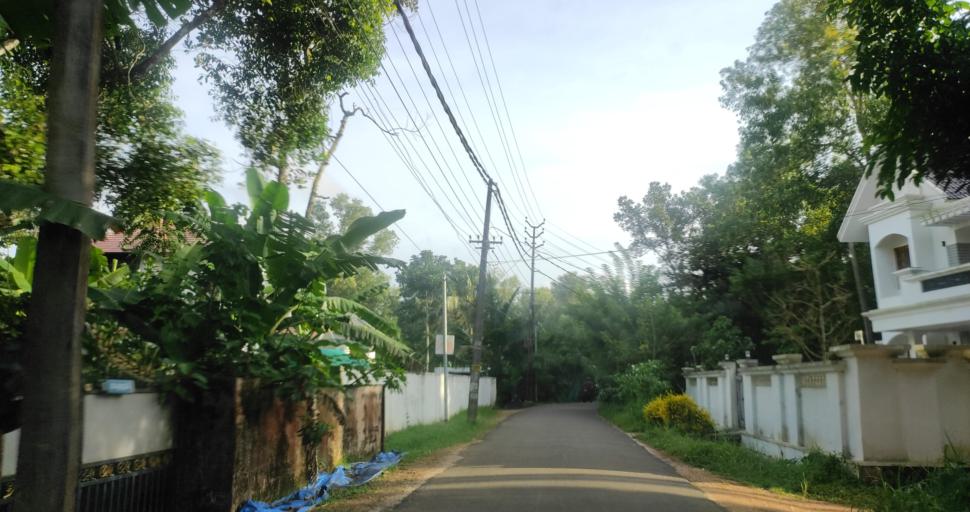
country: IN
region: Kerala
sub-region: Alappuzha
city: Shertallai
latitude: 9.6452
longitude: 76.3456
